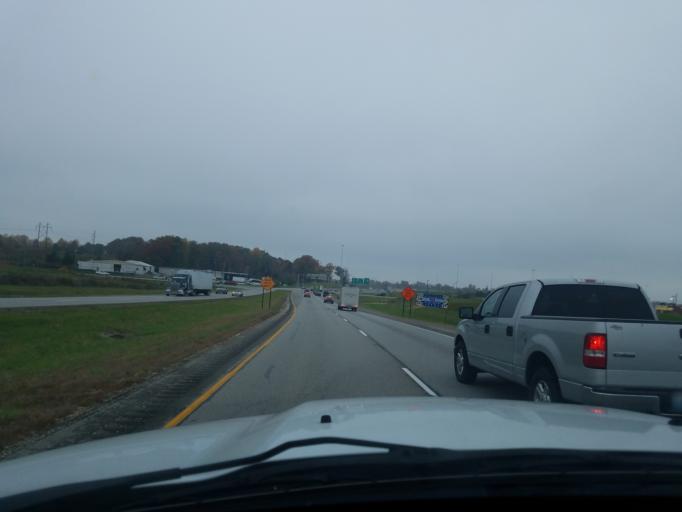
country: US
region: Kentucky
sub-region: Hardin County
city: Elizabethtown
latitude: 37.6690
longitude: -85.8439
